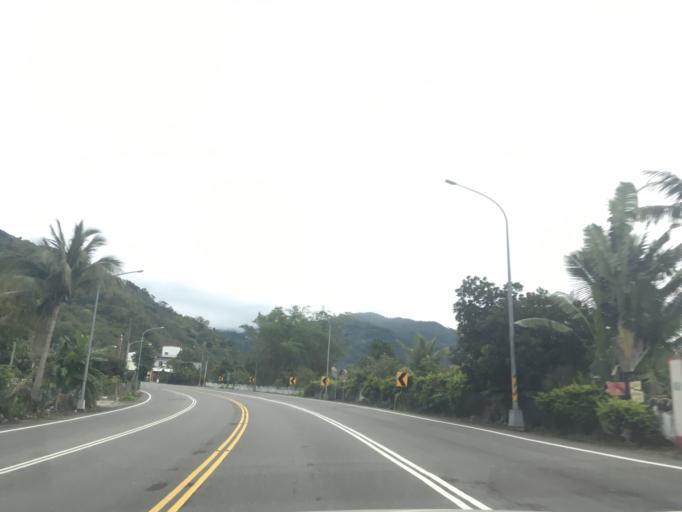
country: TW
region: Taiwan
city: Taitung City
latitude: 22.7470
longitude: 121.0568
